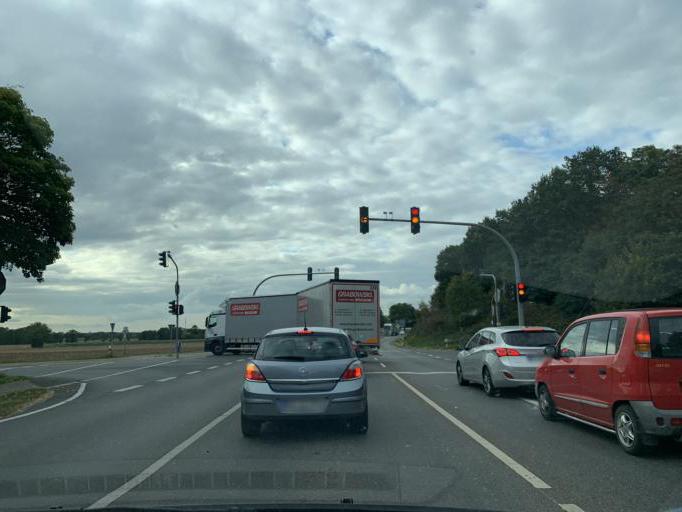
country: DE
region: North Rhine-Westphalia
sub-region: Regierungsbezirk Koln
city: Wassenberg
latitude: 51.0930
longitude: 6.1523
